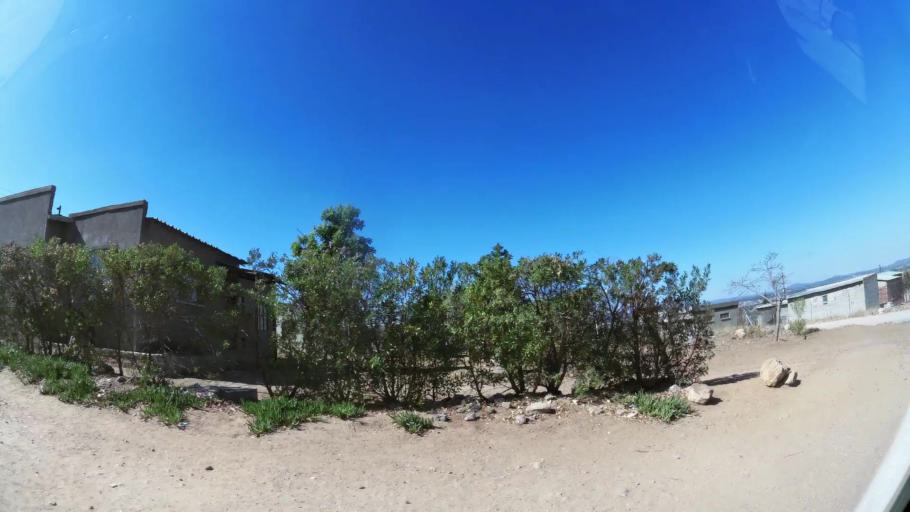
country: ZA
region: Limpopo
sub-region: Capricorn District Municipality
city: Polokwane
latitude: -23.8814
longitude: 29.4102
